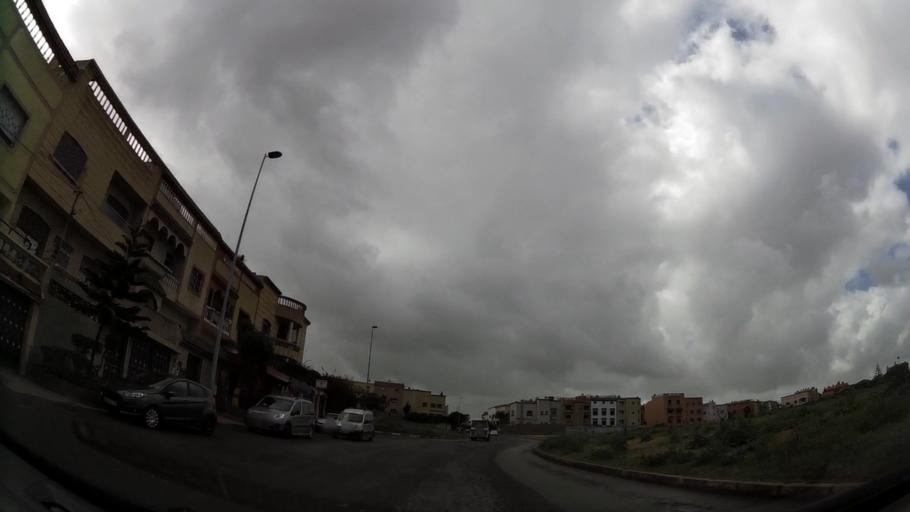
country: MA
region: Grand Casablanca
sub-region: Casablanca
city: Casablanca
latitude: 33.5317
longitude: -7.5935
